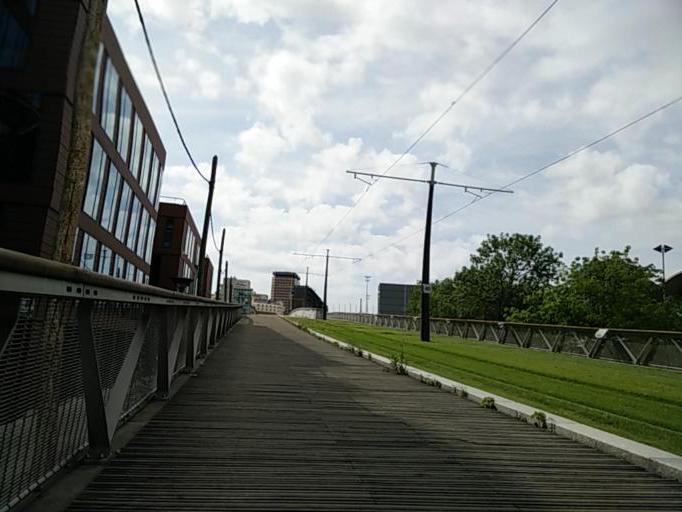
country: FR
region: Ile-de-France
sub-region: Departement de Seine-Saint-Denis
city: Pantin
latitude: 48.8971
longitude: 2.3962
